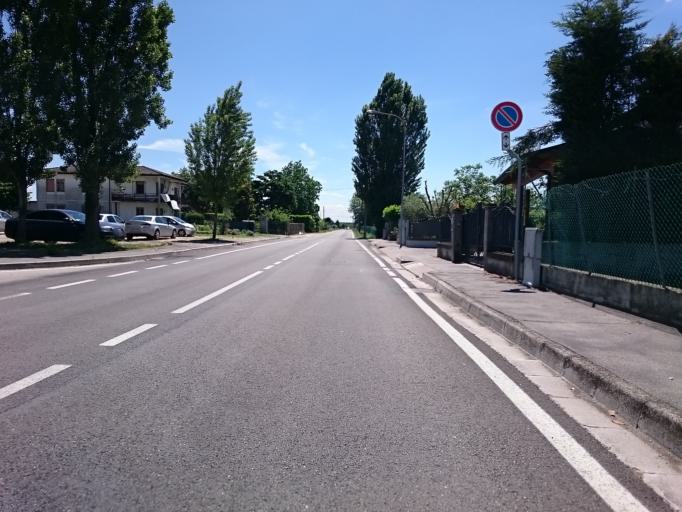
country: IT
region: Veneto
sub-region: Provincia di Padova
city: Campagnola
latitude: 45.2752
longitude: 12.0002
